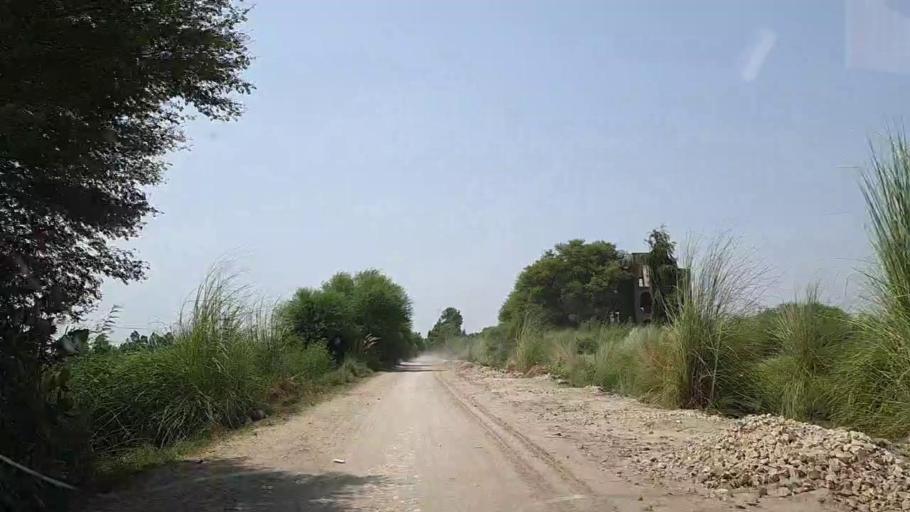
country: PK
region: Sindh
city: Ghotki
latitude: 28.0864
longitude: 69.3379
